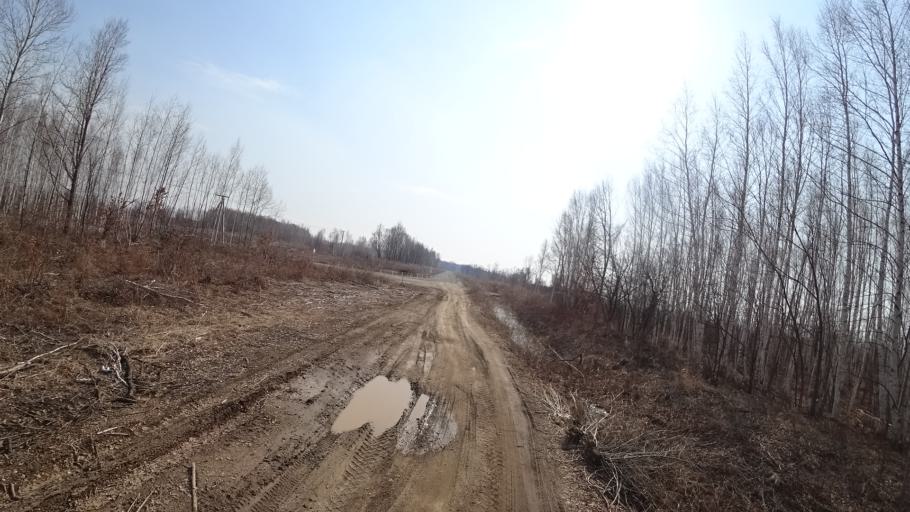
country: RU
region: Amur
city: Novobureyskiy
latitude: 49.8284
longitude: 129.9891
